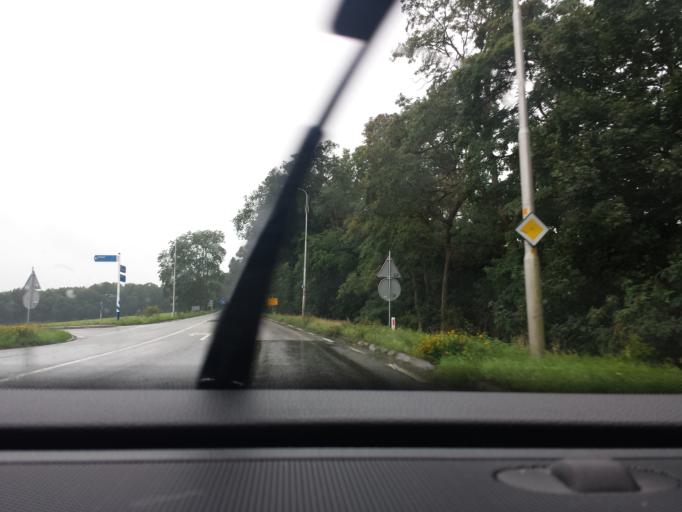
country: NL
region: Gelderland
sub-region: Gemeente Montferland
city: s-Heerenberg
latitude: 51.8973
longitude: 6.2575
